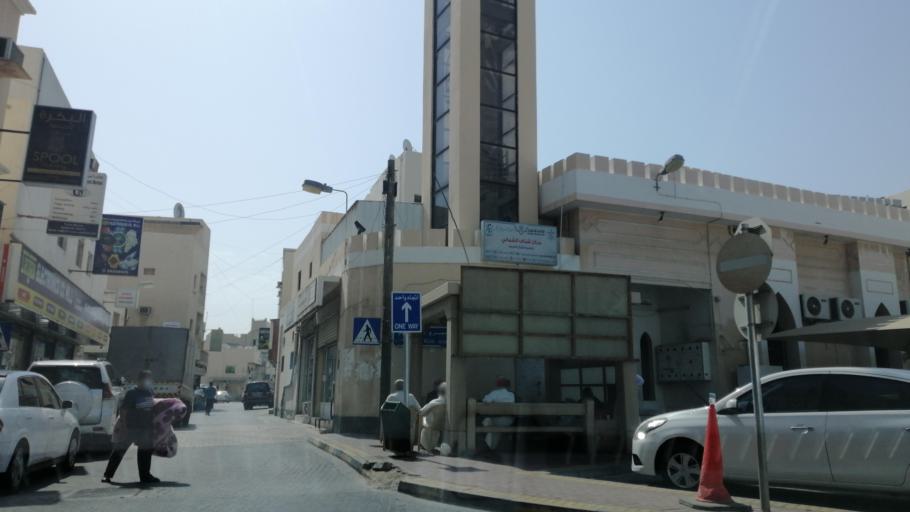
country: BH
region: Muharraq
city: Al Hadd
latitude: 26.2469
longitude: 50.6542
